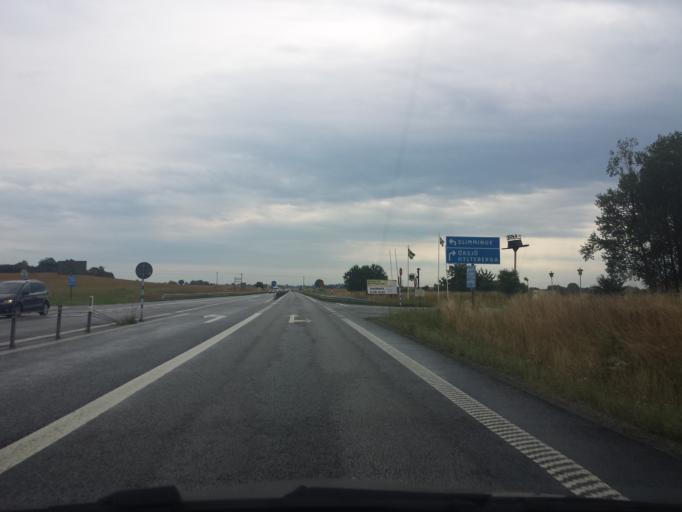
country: SE
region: Skane
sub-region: Skurups Kommun
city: Rydsgard
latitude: 55.4880
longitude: 13.5499
